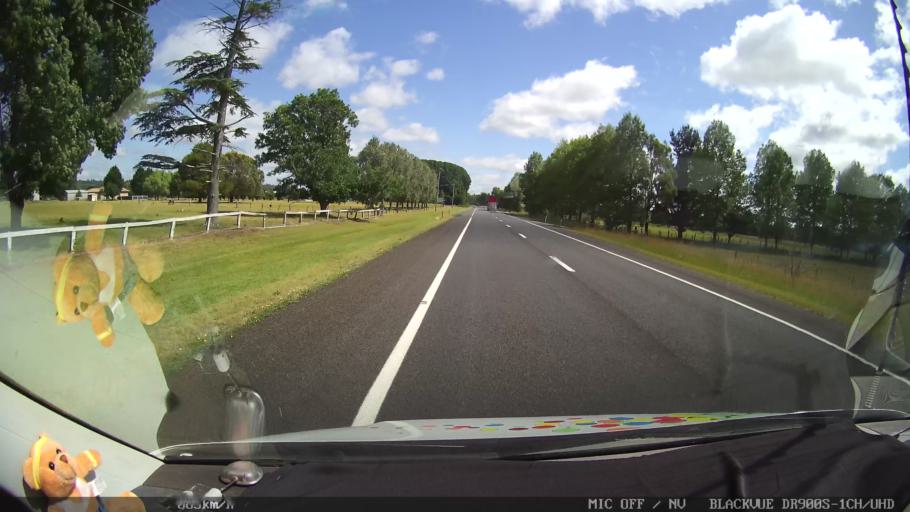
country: AU
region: New South Wales
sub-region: Glen Innes Severn
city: Glen Innes
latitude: -29.8176
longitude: 151.7407
